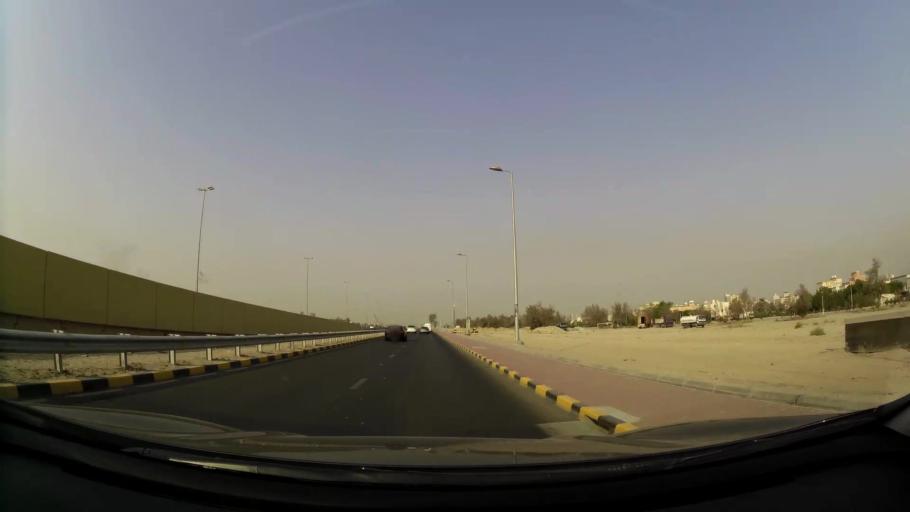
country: KW
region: Al Asimah
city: Ar Rabiyah
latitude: 29.3115
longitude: 47.8255
